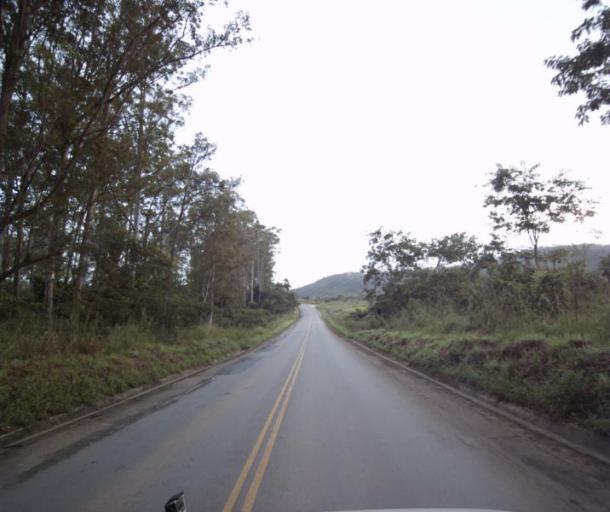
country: BR
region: Goias
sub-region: Pirenopolis
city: Pirenopolis
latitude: -15.8544
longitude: -48.7657
